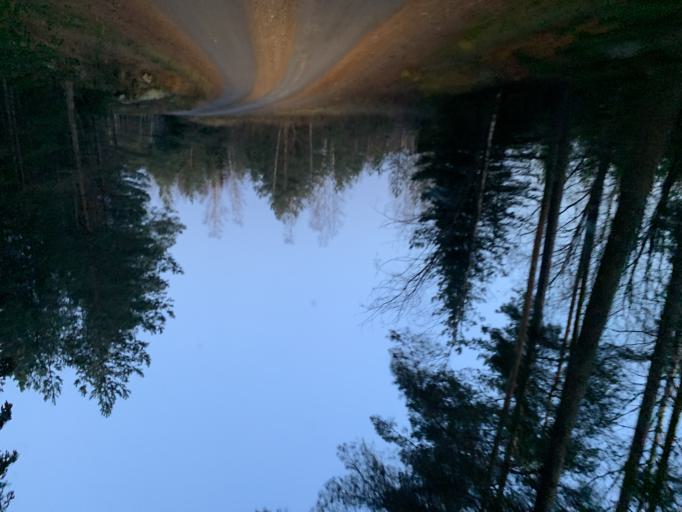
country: SE
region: OErebro
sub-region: Lindesbergs Kommun
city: Fellingsbro
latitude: 59.3424
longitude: 15.5406
